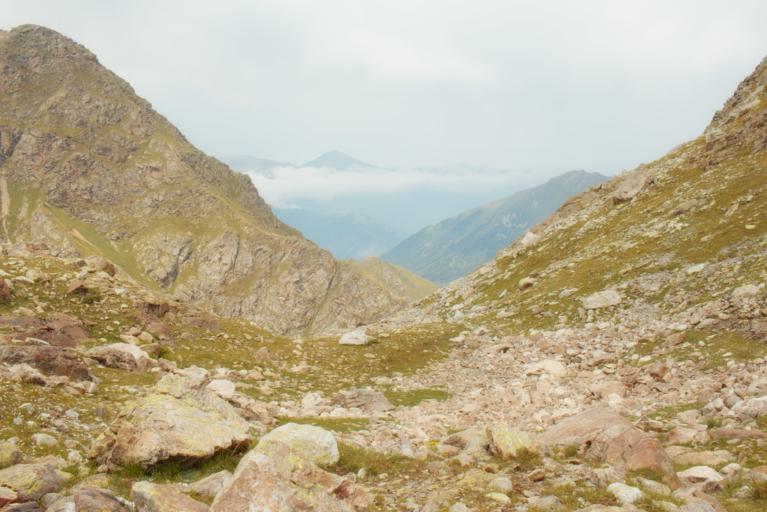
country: RU
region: Karachayevo-Cherkesiya
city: Nizhniy Arkhyz
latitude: 43.4510
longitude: 41.2347
